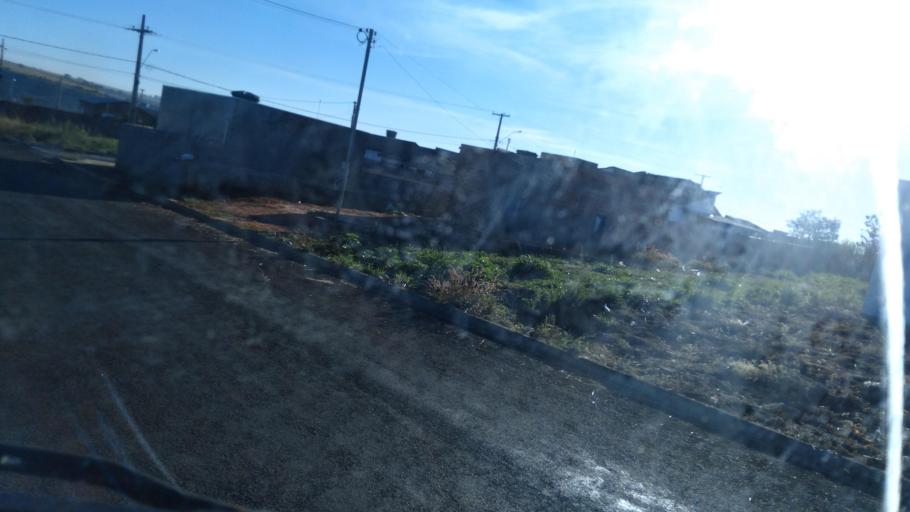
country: BR
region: Goias
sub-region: Mineiros
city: Mineiros
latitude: -17.5421
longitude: -52.5528
